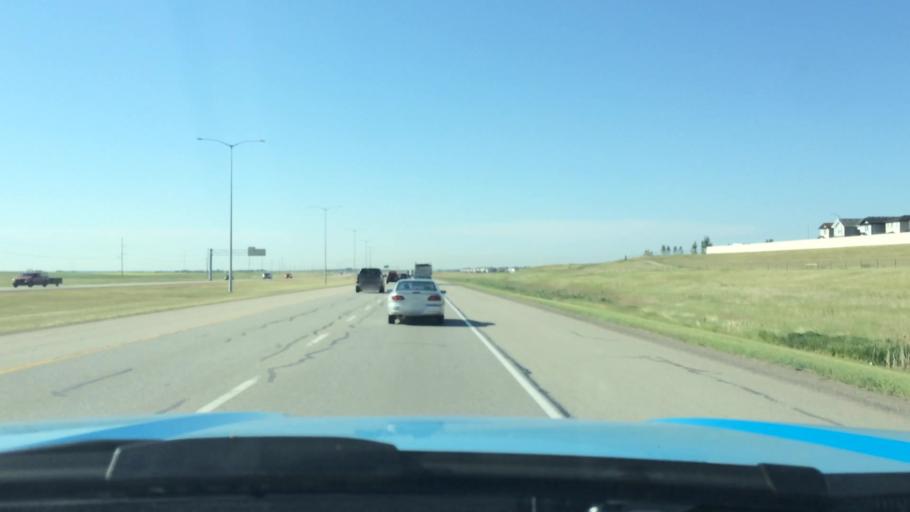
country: CA
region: Alberta
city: Chestermere
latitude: 51.1211
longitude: -113.9216
